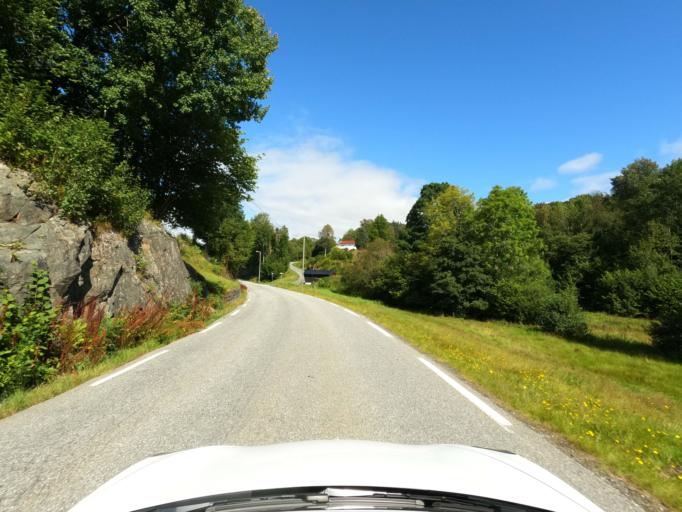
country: NO
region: Hordaland
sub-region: Os
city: Hagavik
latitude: 60.1640
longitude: 5.3406
